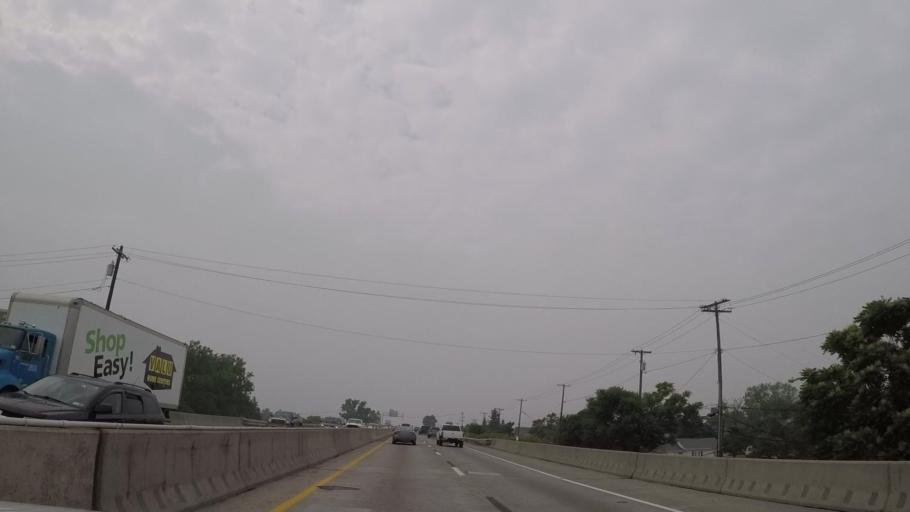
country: US
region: New York
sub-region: Erie County
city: Kenmore
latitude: 42.9402
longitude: -78.9063
